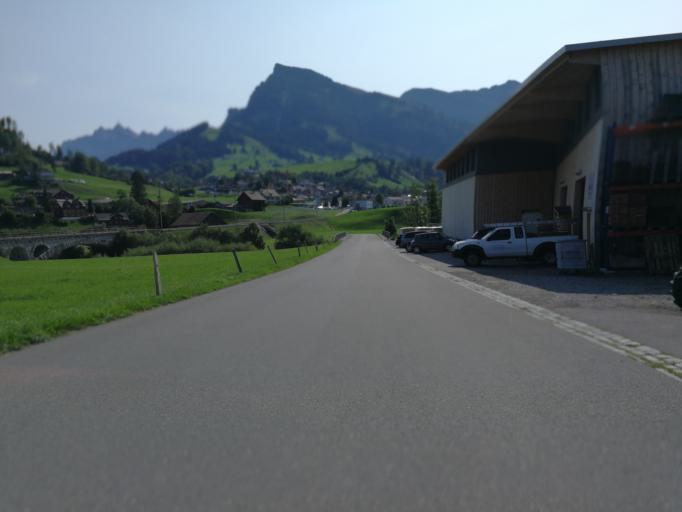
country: CH
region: Saint Gallen
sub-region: Wahlkreis Toggenburg
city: Krummenau
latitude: 47.2334
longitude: 9.1837
